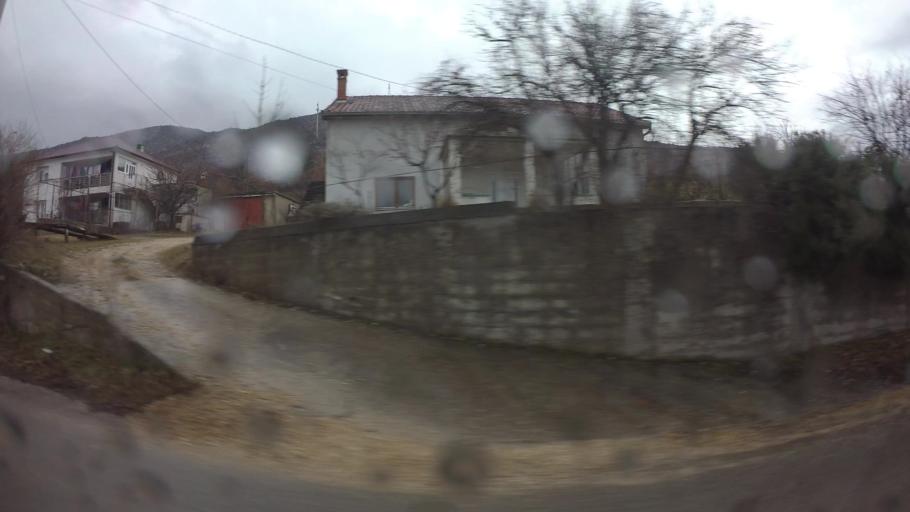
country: BA
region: Federation of Bosnia and Herzegovina
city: Blagaj
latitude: 43.2962
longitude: 17.8564
